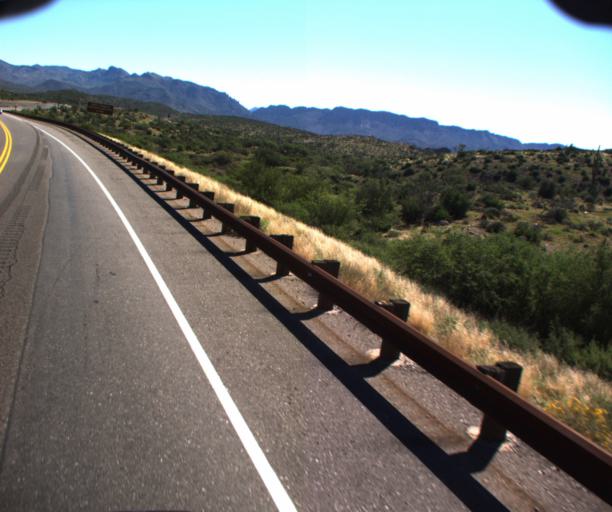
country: US
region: Arizona
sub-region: Pinal County
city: Superior
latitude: 33.2774
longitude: -111.1745
